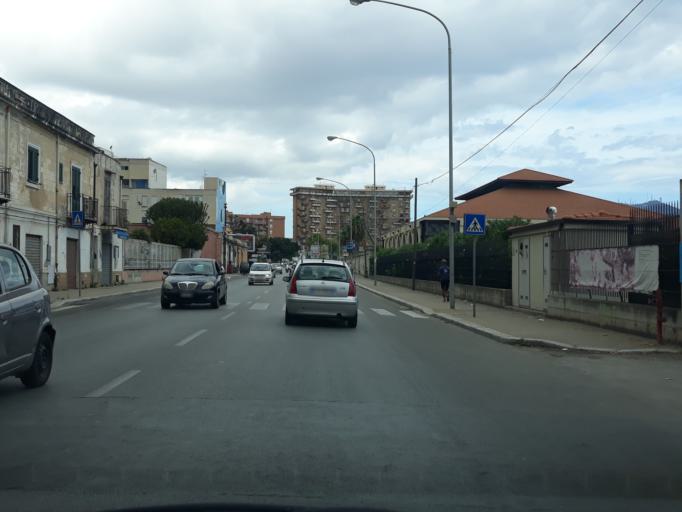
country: IT
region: Sicily
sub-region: Palermo
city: Ciaculli
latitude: 38.1083
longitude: 13.3811
